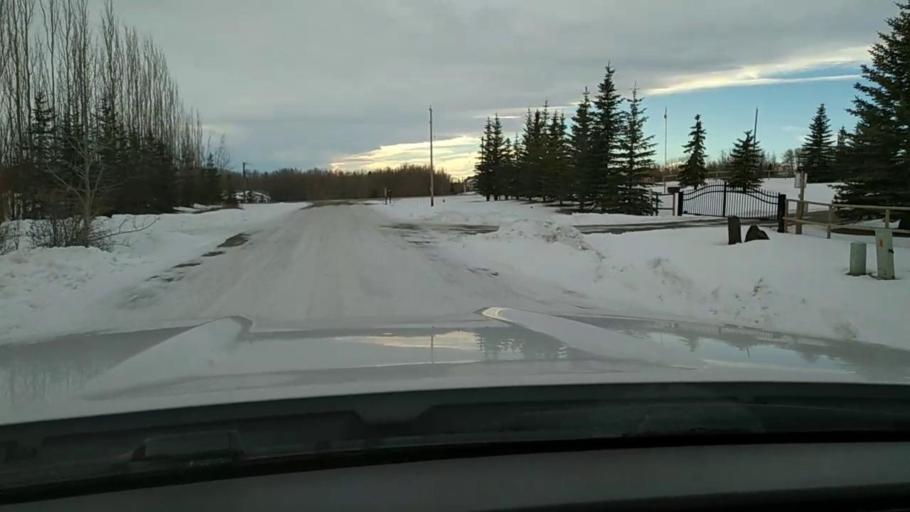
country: CA
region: Alberta
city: Calgary
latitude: 51.1732
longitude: -114.2446
